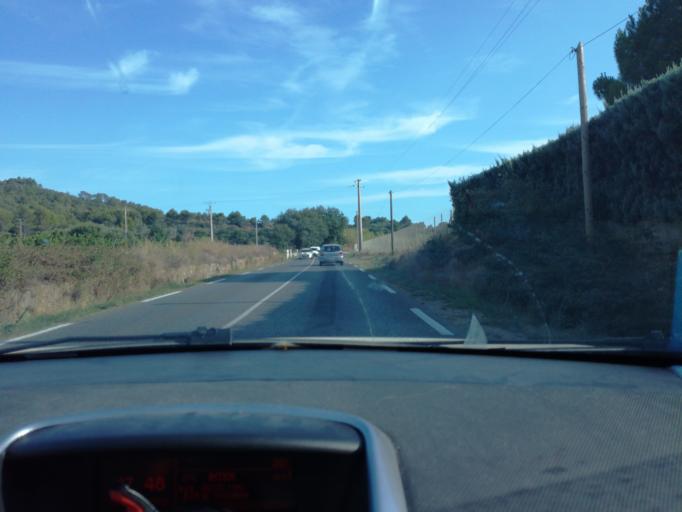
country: FR
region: Provence-Alpes-Cote d'Azur
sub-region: Departement du Var
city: La Crau
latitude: 43.1416
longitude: 6.0803
